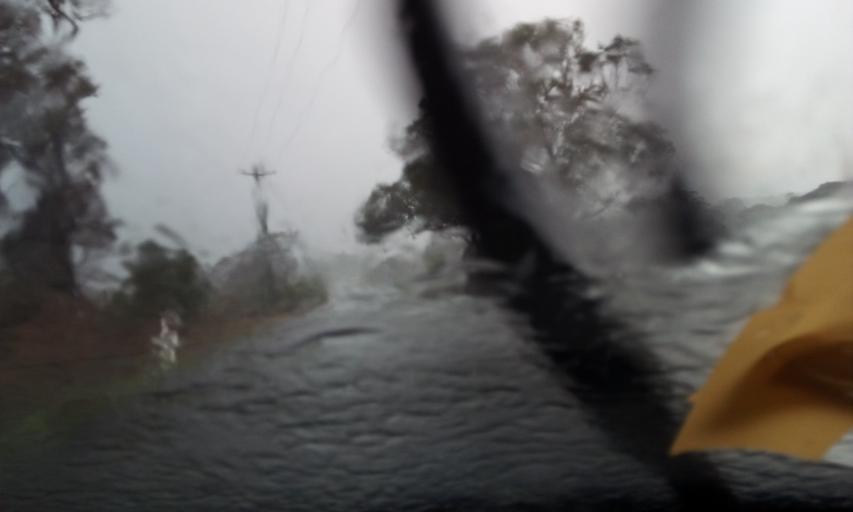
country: AU
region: New South Wales
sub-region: Wollondilly
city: Douglas Park
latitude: -34.1527
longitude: 150.7221
